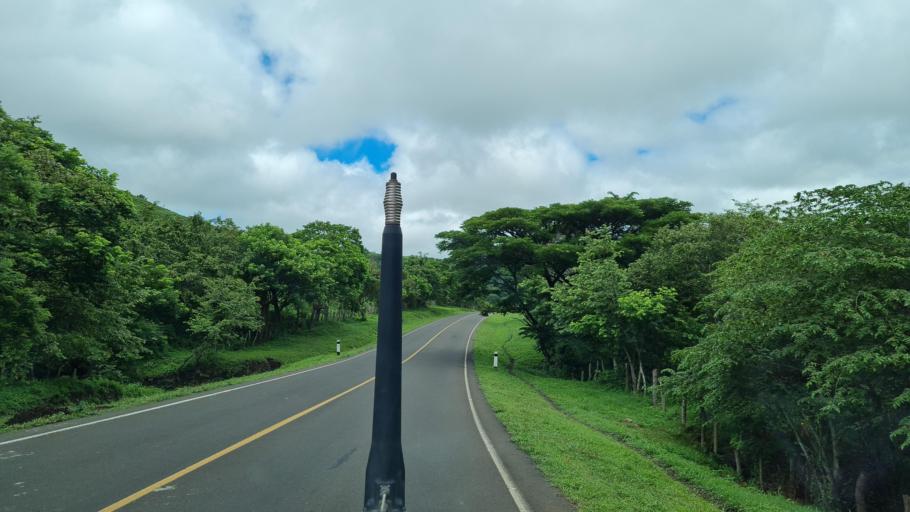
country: NI
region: Matagalpa
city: Terrabona
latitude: 12.5925
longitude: -85.9349
